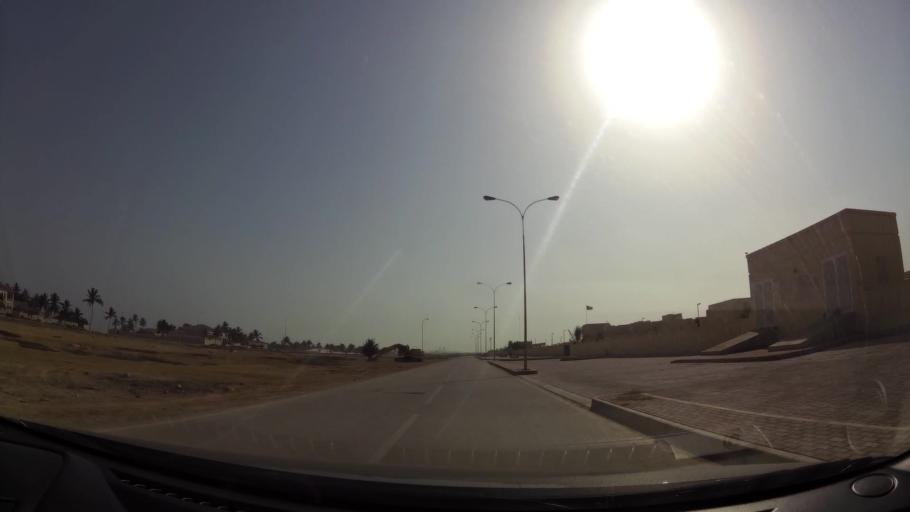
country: OM
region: Zufar
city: Salalah
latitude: 16.9943
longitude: 54.0485
